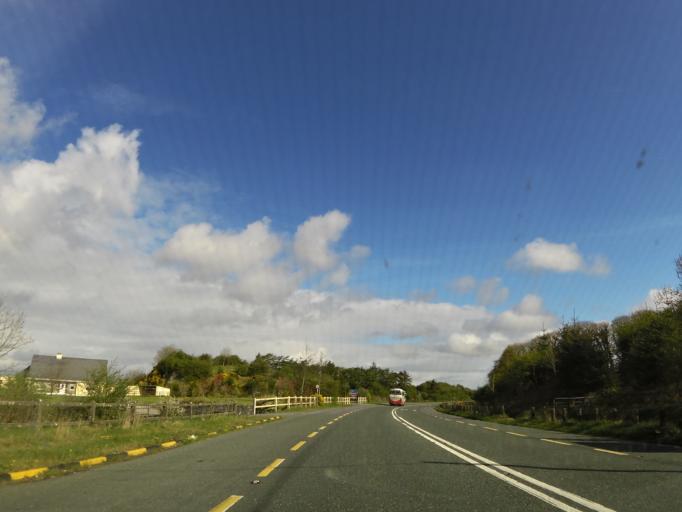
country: IE
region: Connaught
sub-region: Maigh Eo
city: Ballyhaunis
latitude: 53.8611
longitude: -8.8549
